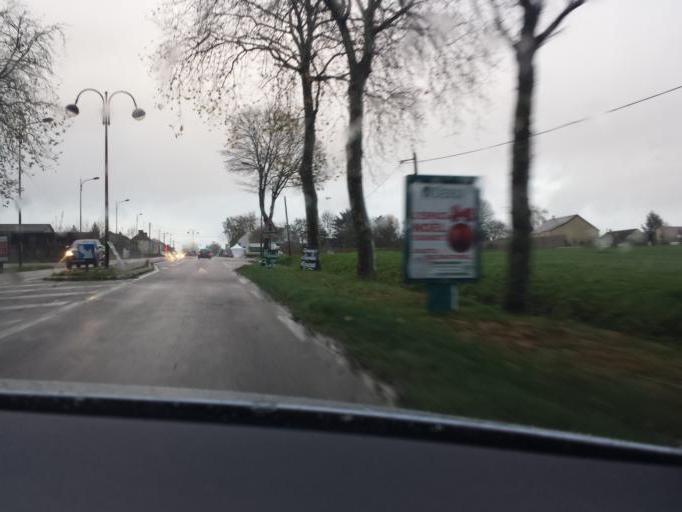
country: FR
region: Haute-Normandie
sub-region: Departement de l'Eure
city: Breuilpont
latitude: 49.0188
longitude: 1.4798
